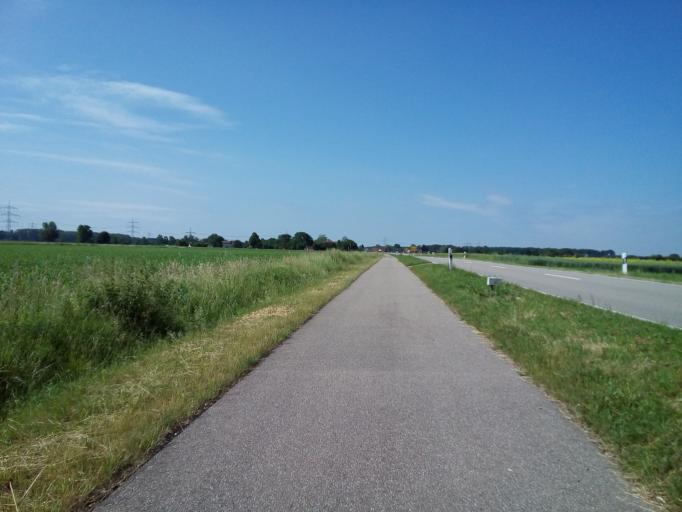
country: DE
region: Baden-Wuerttemberg
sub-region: Freiburg Region
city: Rheinau
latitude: 48.6362
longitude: 7.9227
